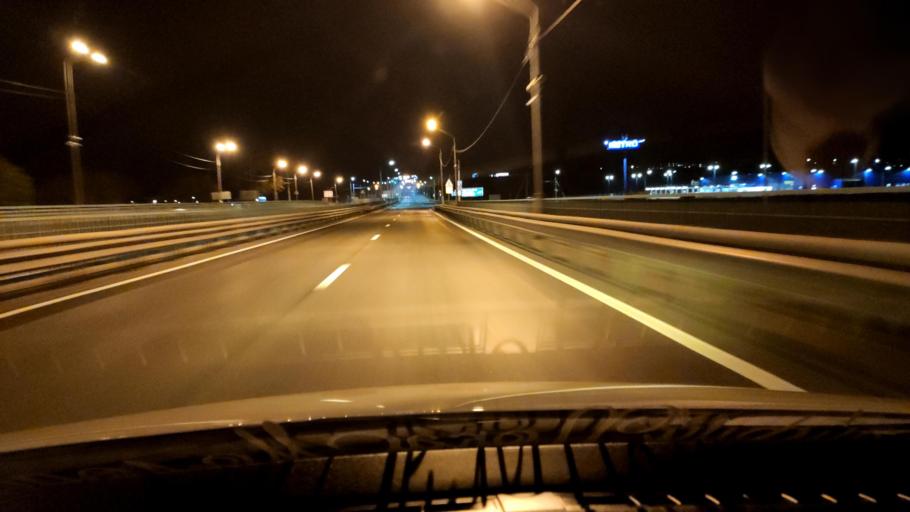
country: RU
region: Voronezj
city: Pridonskoy
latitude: 51.6511
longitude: 39.0669
